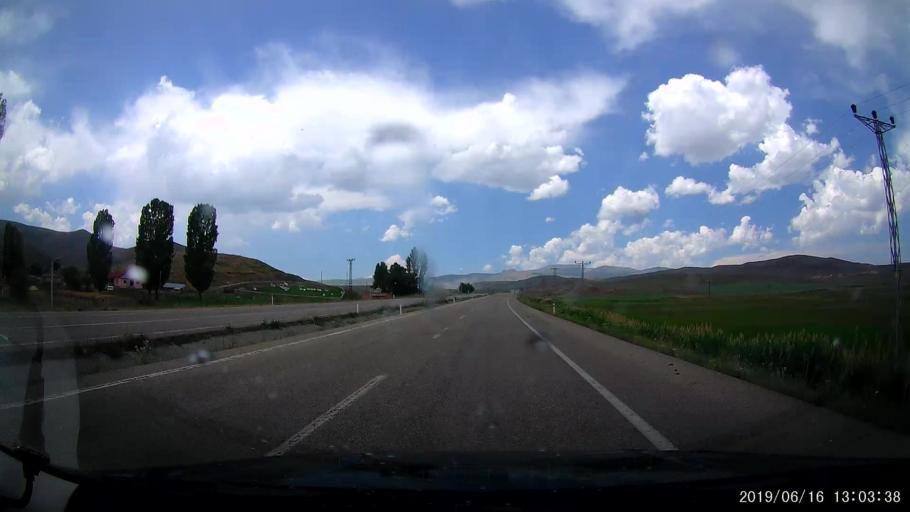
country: TR
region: Agri
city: Sulucem
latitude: 39.5835
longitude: 43.7867
